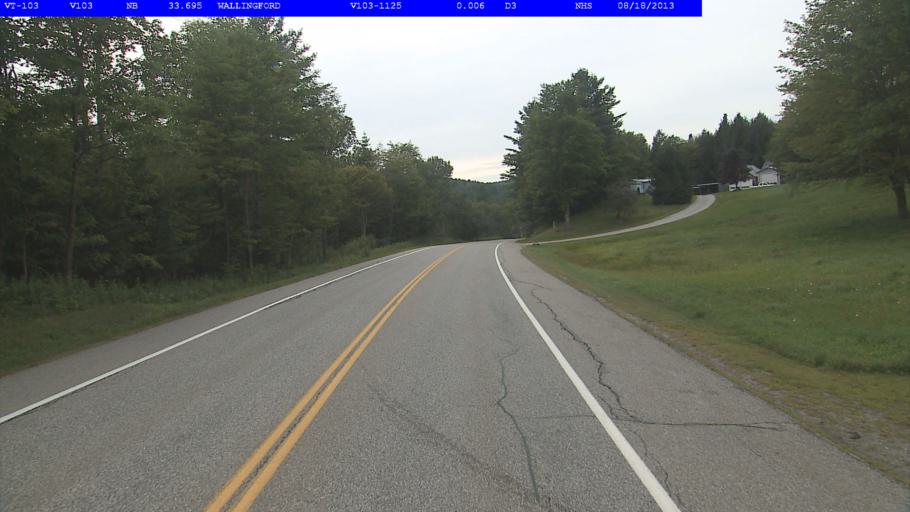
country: US
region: Vermont
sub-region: Rutland County
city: Rutland
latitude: 43.4493
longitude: -72.8729
